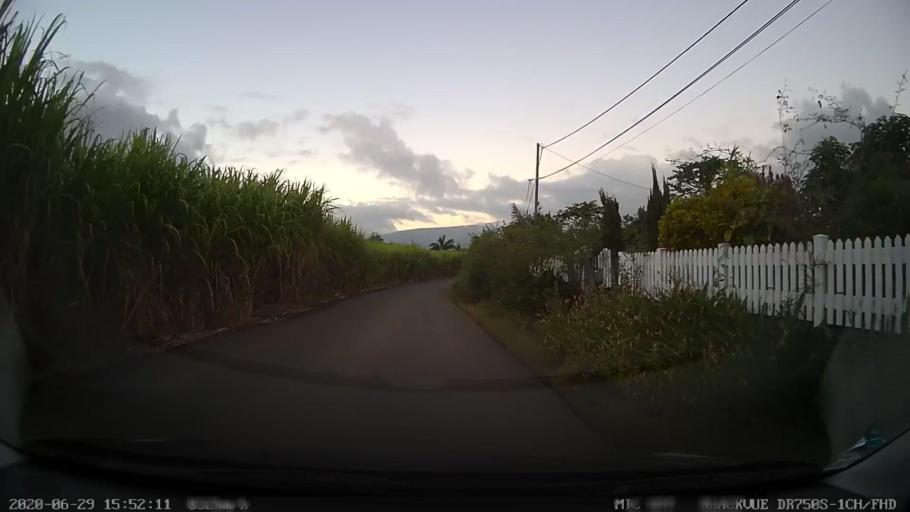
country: RE
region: Reunion
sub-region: Reunion
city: Bras-Panon
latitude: -20.9966
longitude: 55.6941
